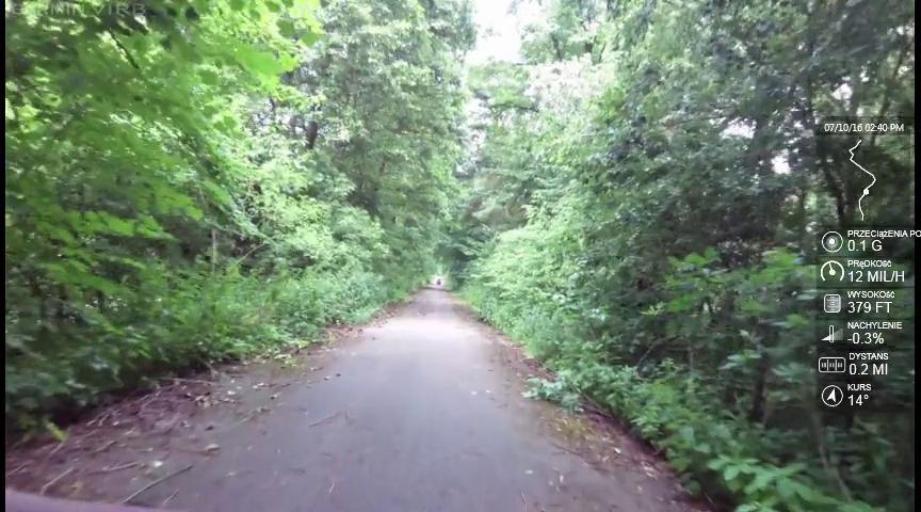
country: PL
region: West Pomeranian Voivodeship
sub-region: Powiat gryfinski
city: Banie
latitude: 53.0793
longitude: 14.6368
